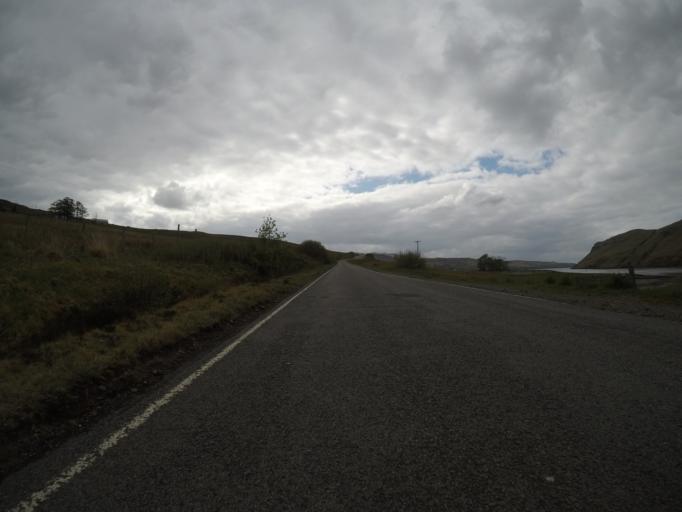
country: GB
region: Scotland
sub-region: Highland
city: Isle of Skye
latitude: 57.2961
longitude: -6.3199
